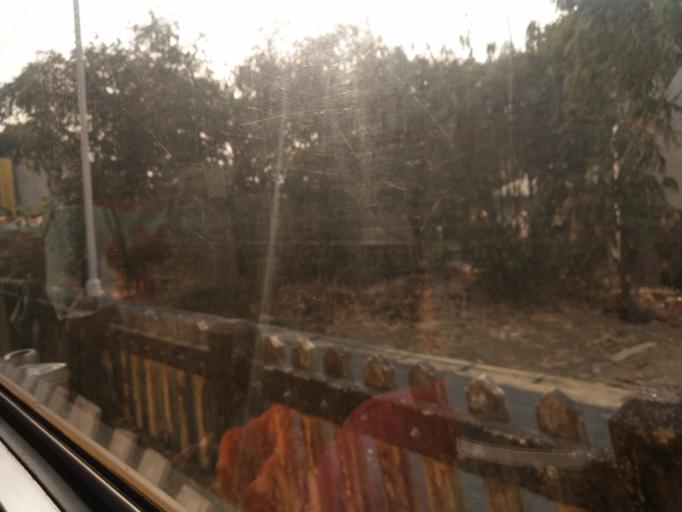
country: TW
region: Taiwan
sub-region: Chiayi
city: Jiayi Shi
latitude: 23.5205
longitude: 120.5489
